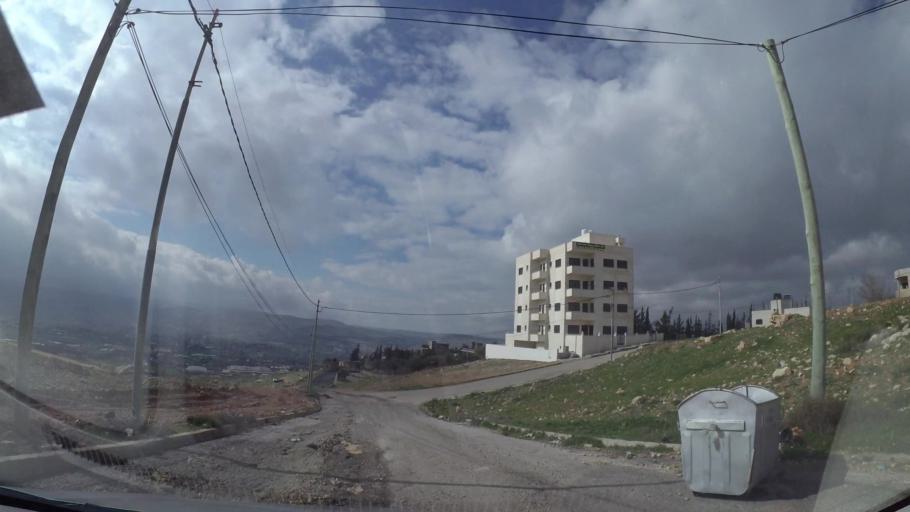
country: JO
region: Amman
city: Al Jubayhah
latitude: 32.0606
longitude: 35.8612
